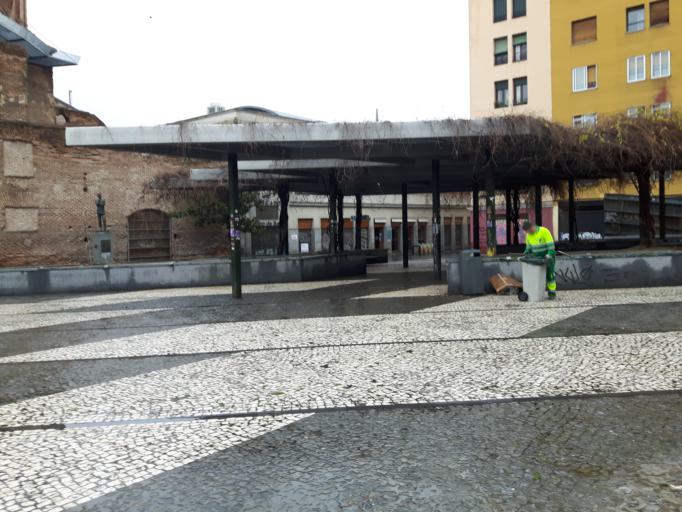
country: ES
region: Madrid
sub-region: Provincia de Madrid
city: Madrid
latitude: 40.4083
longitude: -3.7035
